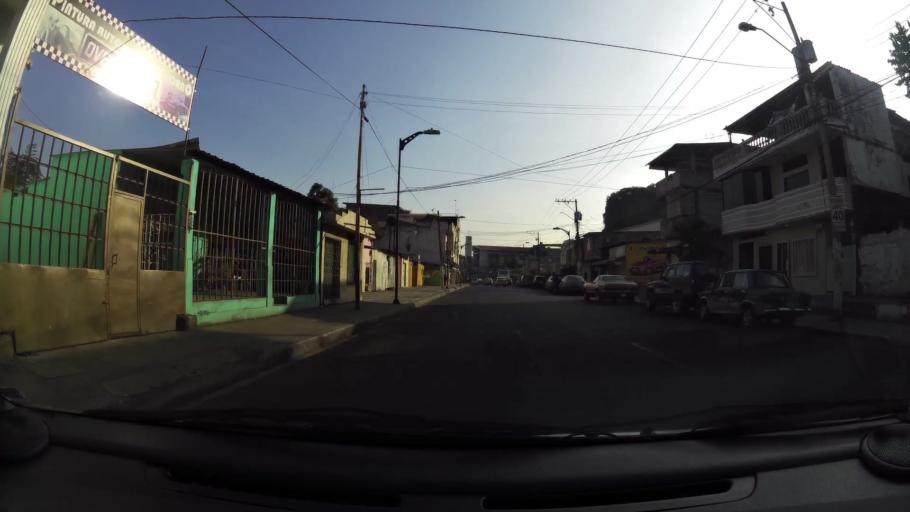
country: EC
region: Guayas
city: Eloy Alfaro
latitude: -2.1751
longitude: -79.8532
